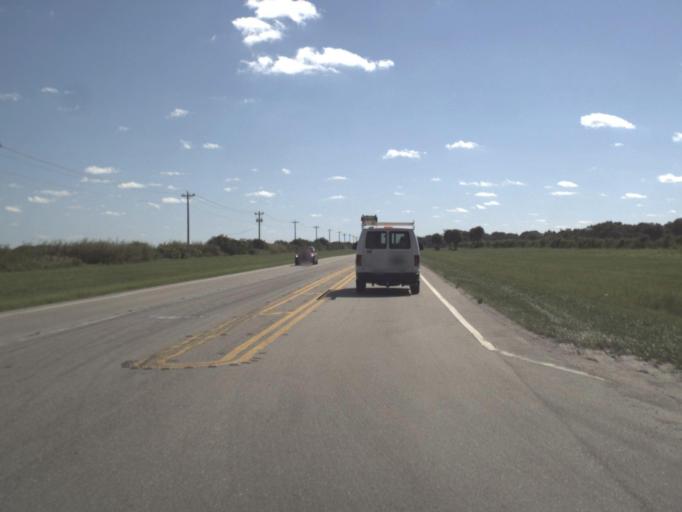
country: US
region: Florida
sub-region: Collier County
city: Immokalee
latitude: 26.4897
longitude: -81.4507
